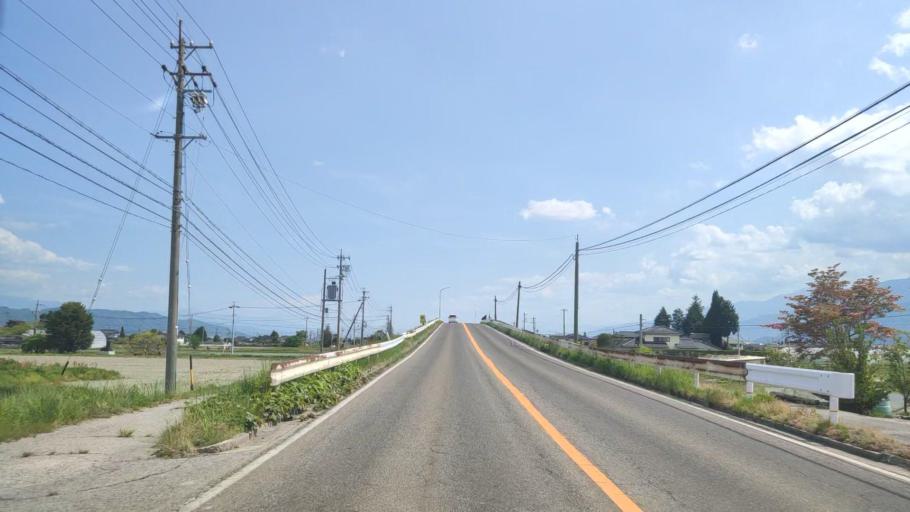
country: JP
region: Nagano
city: Omachi
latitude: 36.4525
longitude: 137.8521
